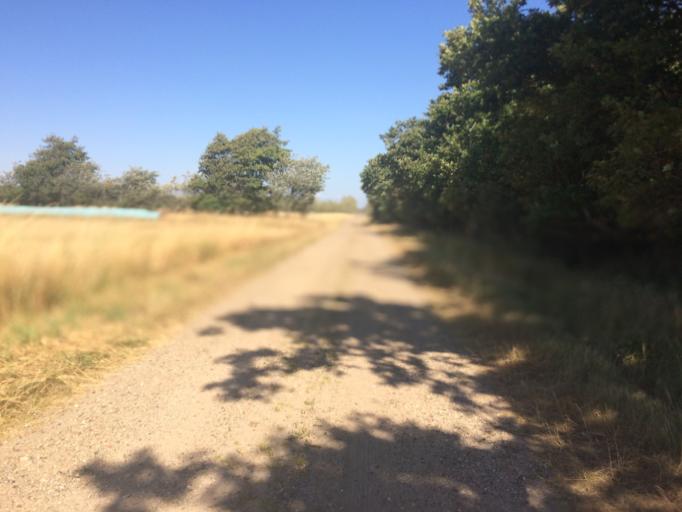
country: DK
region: Central Jutland
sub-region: Holstebro Kommune
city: Vinderup
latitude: 56.5766
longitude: 8.8145
